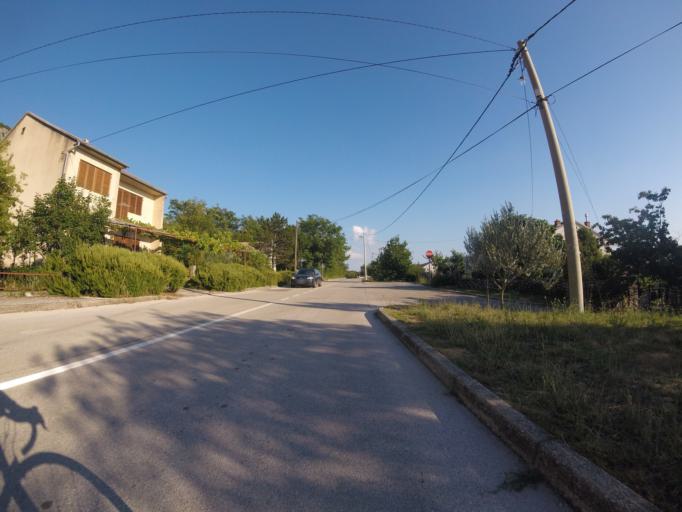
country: HR
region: Primorsko-Goranska
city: Selce
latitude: 45.1894
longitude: 14.7280
